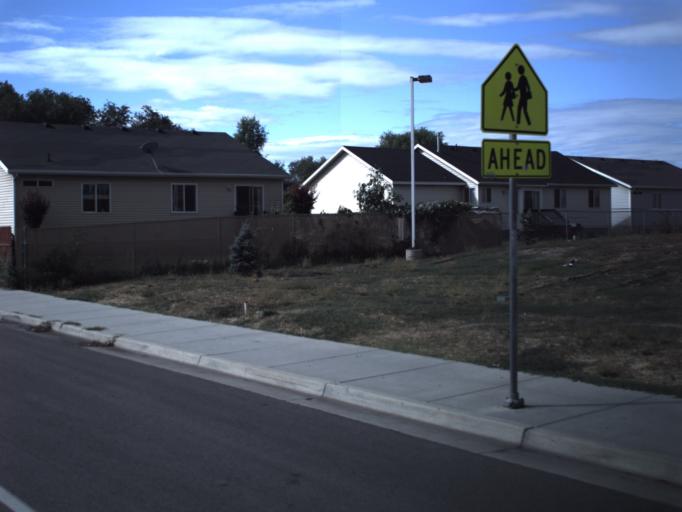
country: US
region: Utah
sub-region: Salt Lake County
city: Salt Lake City
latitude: 40.7922
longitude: -111.9393
